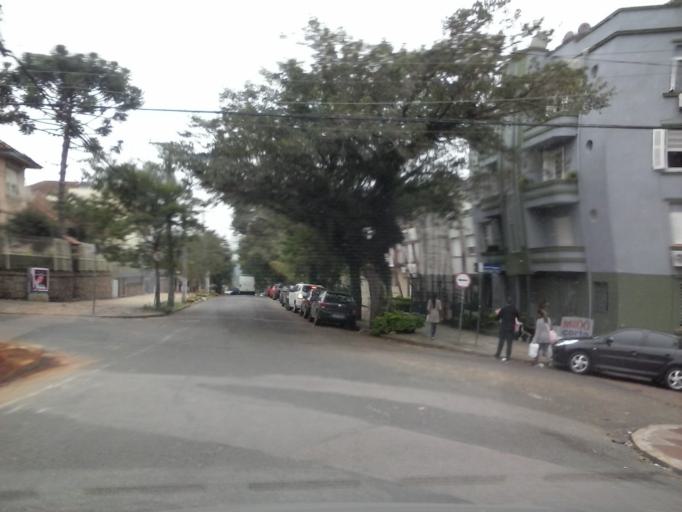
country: BR
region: Rio Grande do Sul
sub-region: Porto Alegre
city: Porto Alegre
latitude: -30.0430
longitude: -51.1828
